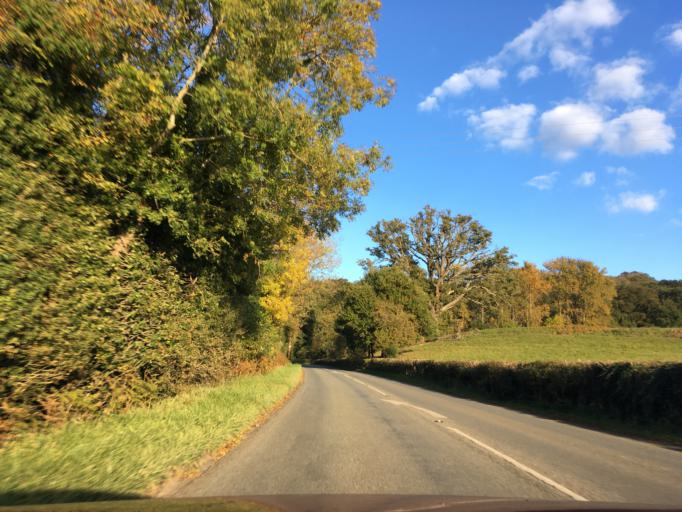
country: GB
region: England
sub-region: Herefordshire
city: Donnington
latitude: 52.0272
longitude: -2.3612
